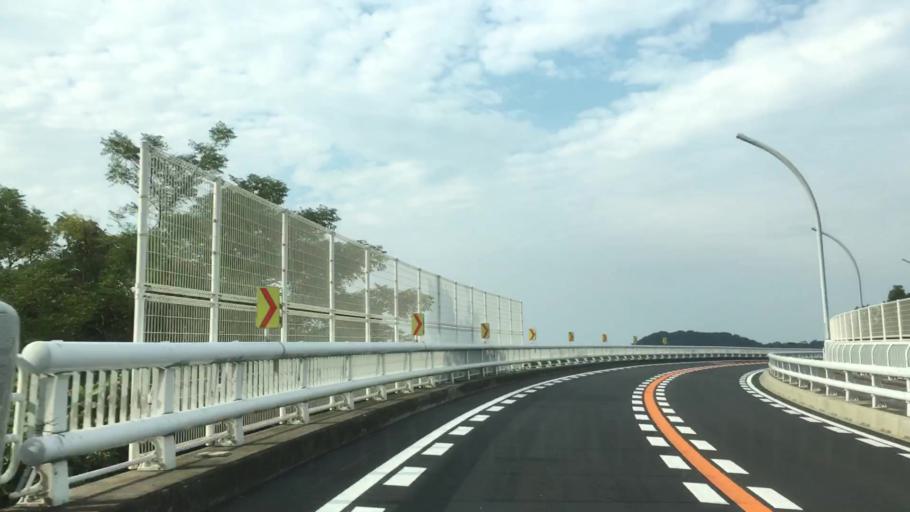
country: JP
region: Nagasaki
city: Sasebo
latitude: 33.0374
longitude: 129.6485
